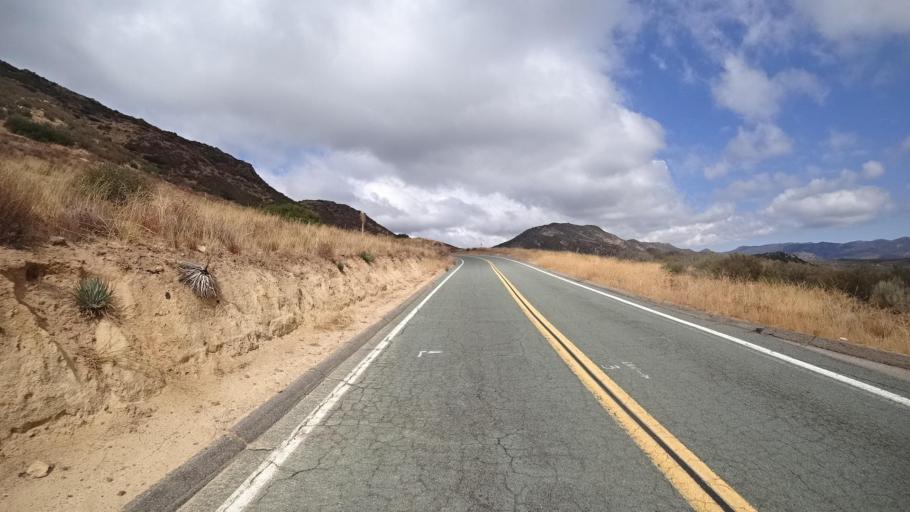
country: US
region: California
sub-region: San Diego County
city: Pine Valley
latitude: 32.7378
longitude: -116.4535
